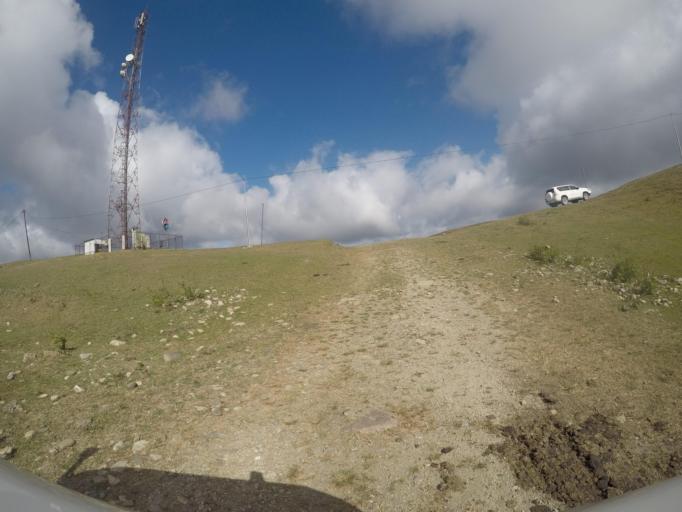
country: TL
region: Lautem
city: Lospalos
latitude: -8.4735
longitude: 126.8709
